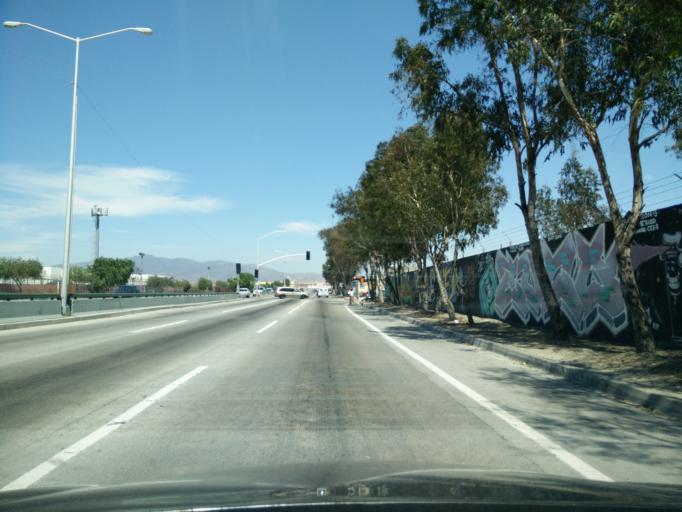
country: MX
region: Baja California
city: Tijuana
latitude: 32.5464
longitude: -116.9814
